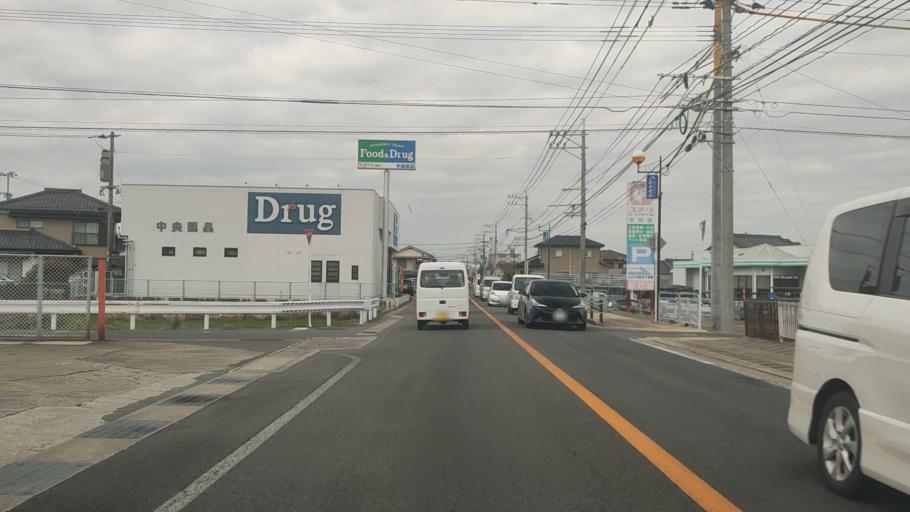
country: JP
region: Nagasaki
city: Shimabara
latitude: 32.8565
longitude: 130.3370
